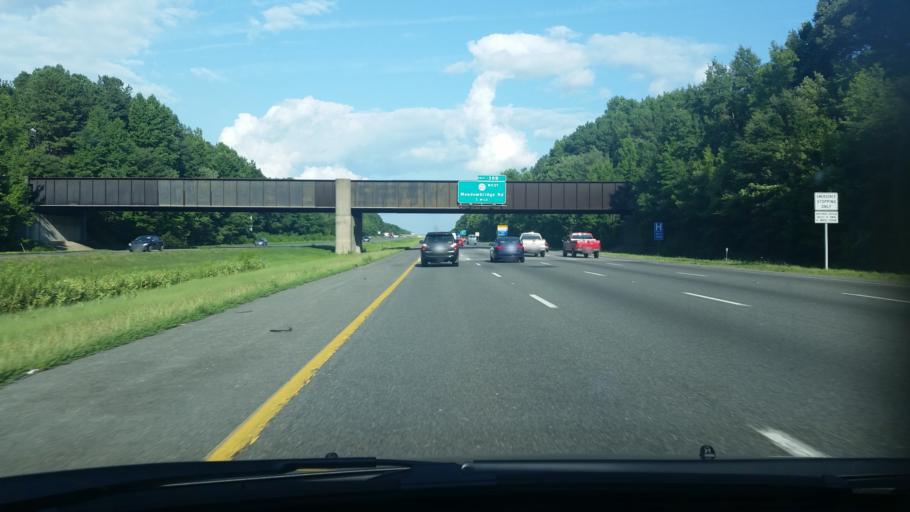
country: US
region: Virginia
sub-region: Henrico County
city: Chamberlayne
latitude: 37.6362
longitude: -77.3991
